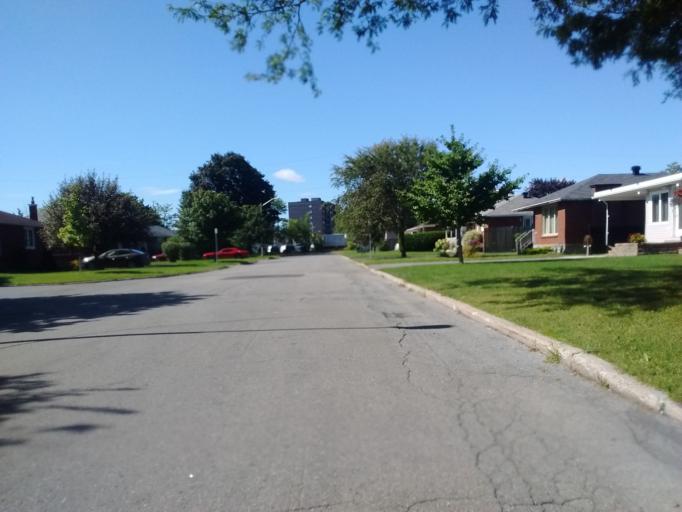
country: CA
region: Ontario
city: Ottawa
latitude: 45.4333
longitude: -75.6399
